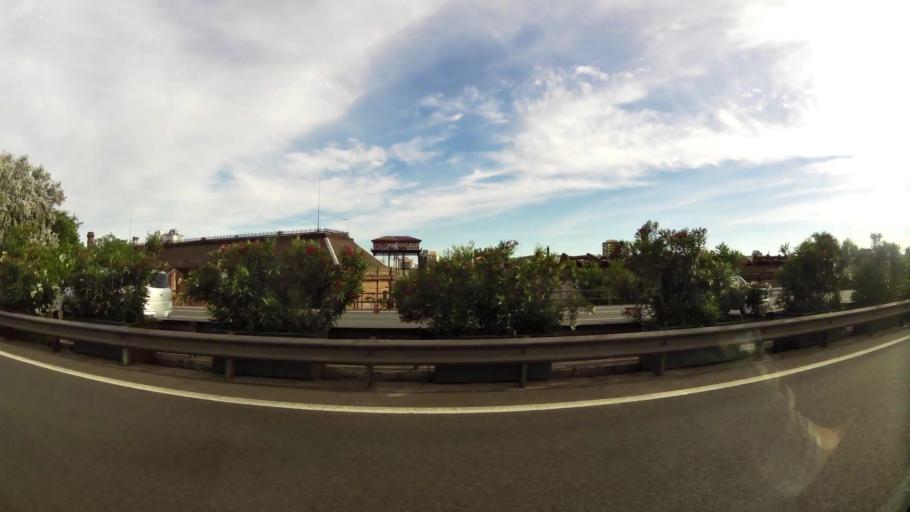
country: AR
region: Buenos Aires F.D.
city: Villa Santa Rita
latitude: -34.6351
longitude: -58.5129
